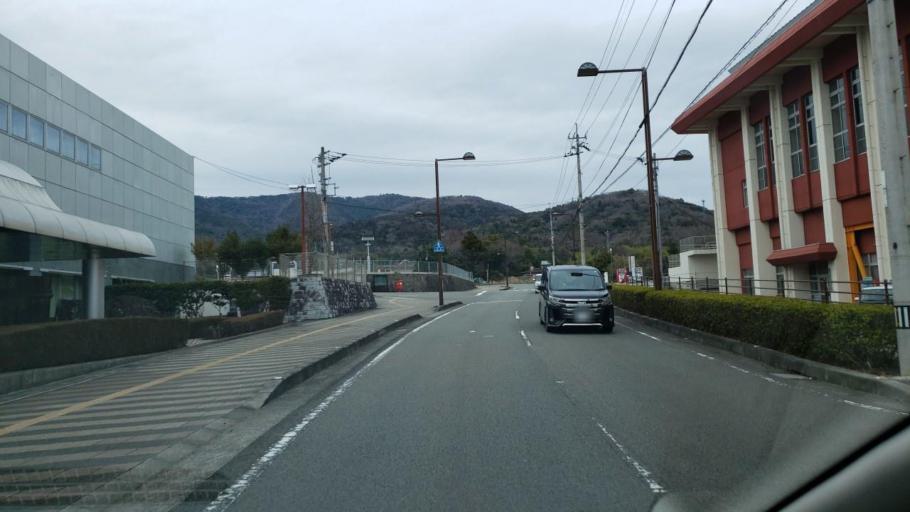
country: JP
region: Tokushima
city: Kamojimacho-jogejima
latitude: 34.1148
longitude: 134.3404
